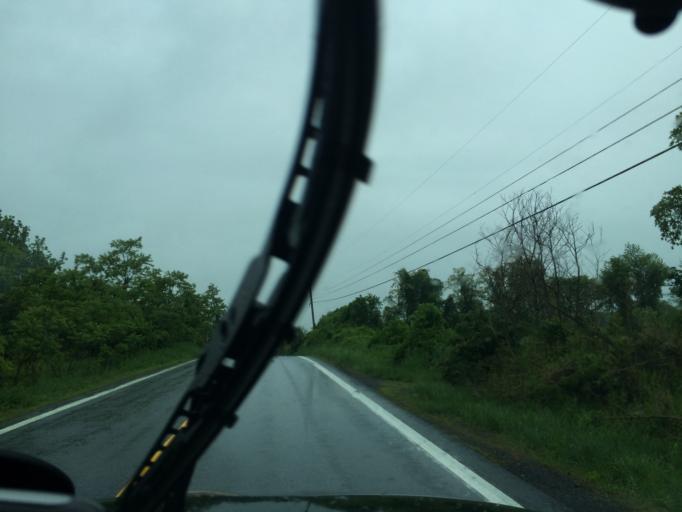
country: US
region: Maryland
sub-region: Washington County
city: Highfield-Cascade
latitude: 39.6915
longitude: -77.4902
